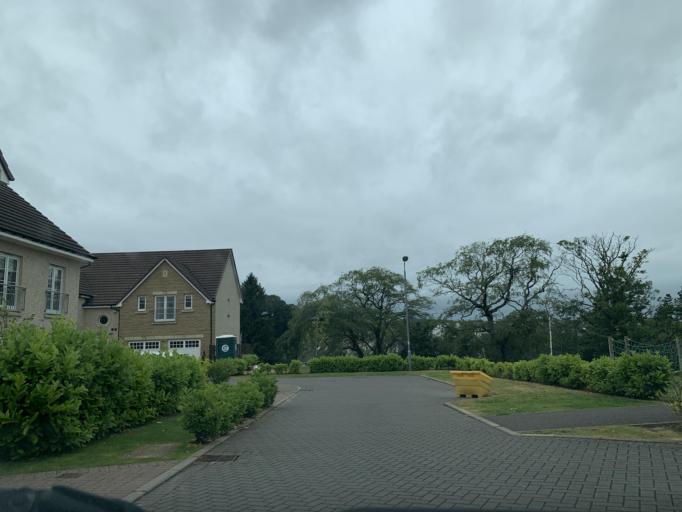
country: GB
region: Scotland
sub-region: East Renfrewshire
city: Newton Mearns
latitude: 55.7893
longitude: -4.3368
